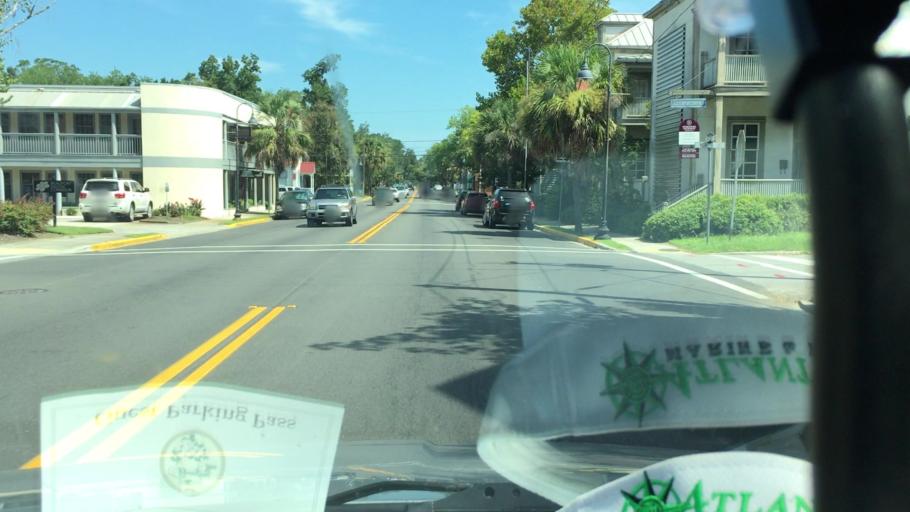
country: US
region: South Carolina
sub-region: Beaufort County
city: Beaufort
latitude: 32.4334
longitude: -80.6699
